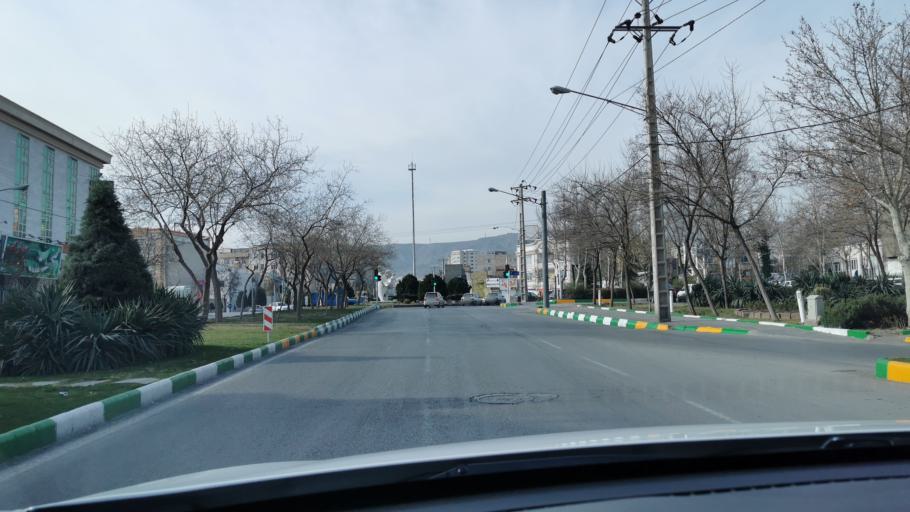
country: IR
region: Razavi Khorasan
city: Mashhad
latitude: 36.3057
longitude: 59.5131
